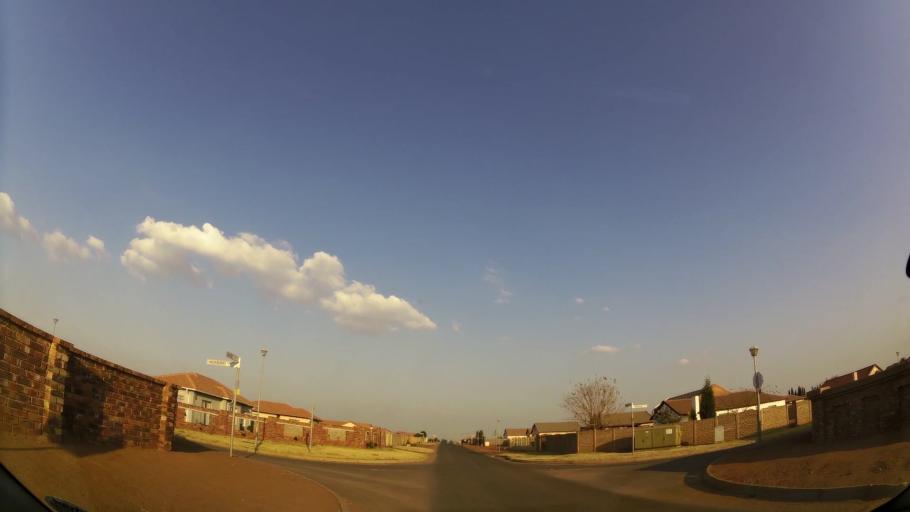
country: ZA
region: Gauteng
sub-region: Ekurhuleni Metropolitan Municipality
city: Benoni
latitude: -26.1257
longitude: 28.3767
